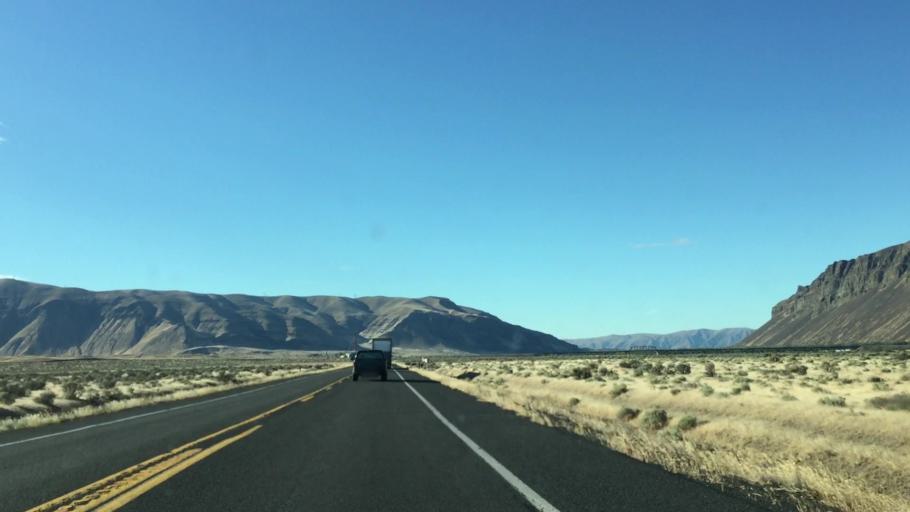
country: US
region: Washington
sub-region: Grant County
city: Mattawa
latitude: 46.8573
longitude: -119.9476
